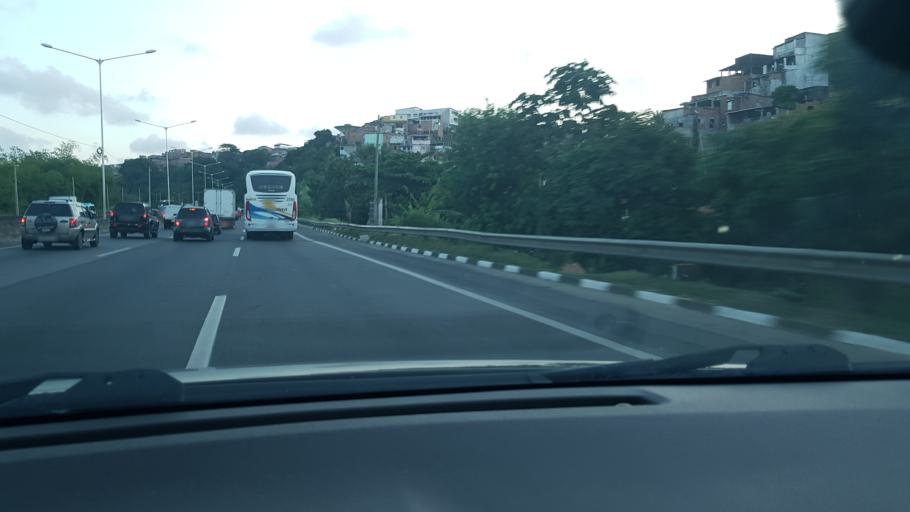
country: BR
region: Bahia
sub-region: Salvador
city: Salvador
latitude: -12.9326
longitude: -38.4715
